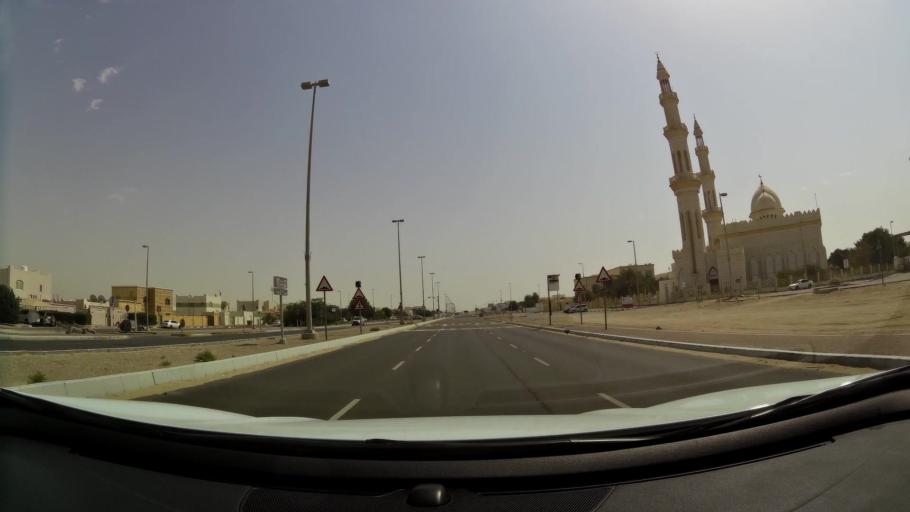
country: AE
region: Abu Dhabi
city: Abu Dhabi
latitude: 24.3011
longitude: 54.6465
